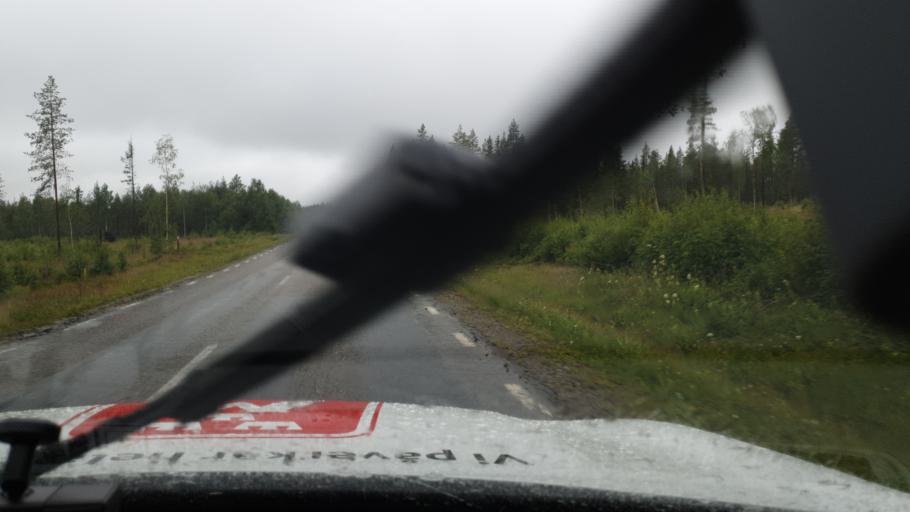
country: SE
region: Vaesterbotten
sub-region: Skelleftea Kommun
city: Langsele
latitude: 65.0290
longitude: 20.2149
